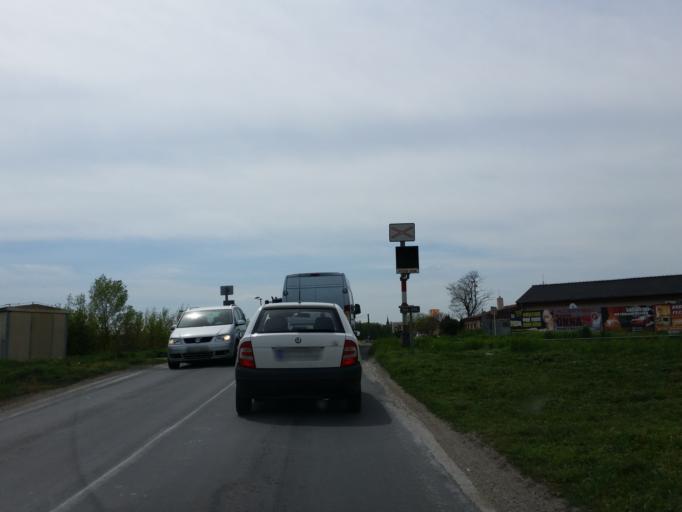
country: SK
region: Trnavsky
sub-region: Okres Dunajska Streda
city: Velky Meder
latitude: 47.8640
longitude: 17.7809
